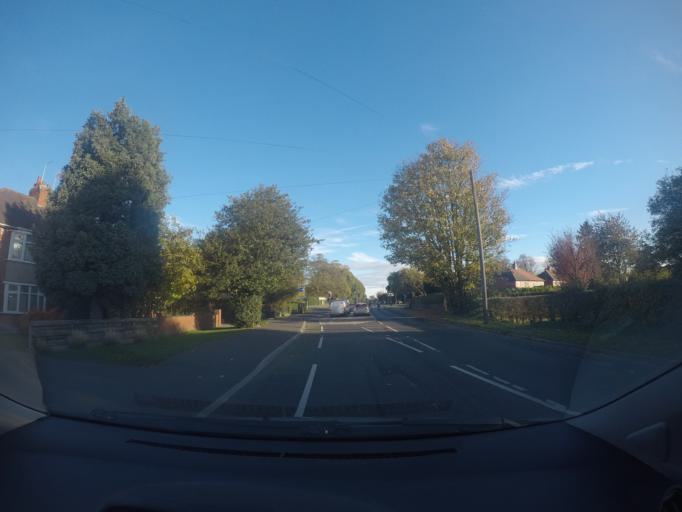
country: GB
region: England
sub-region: City of York
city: Nether Poppleton
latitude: 53.9703
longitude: -1.1345
